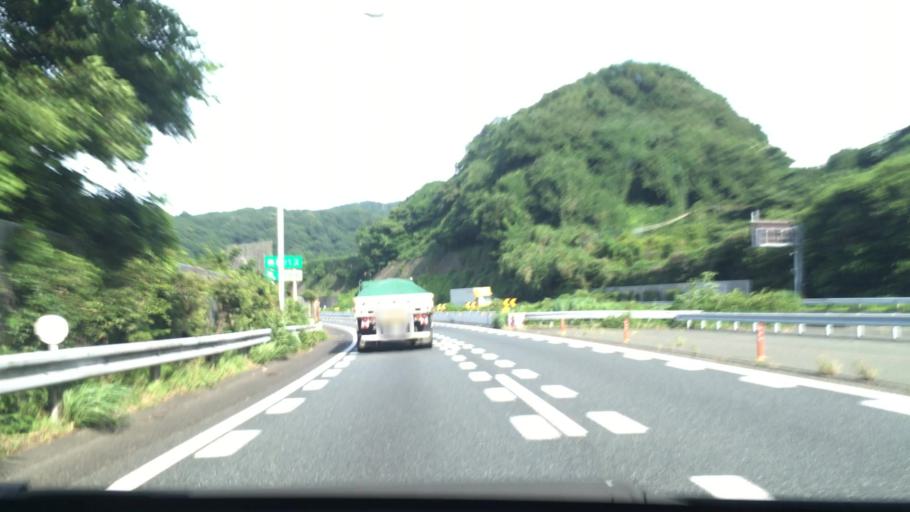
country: JP
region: Yamaguchi
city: Shimonoseki
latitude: 33.9549
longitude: 130.9727
